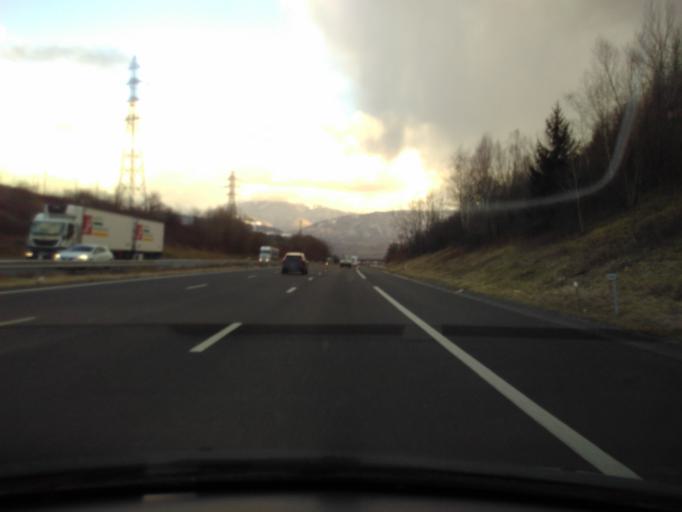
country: FR
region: Rhone-Alpes
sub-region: Departement de la Savoie
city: Les Marches
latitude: 45.5031
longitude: 6.0167
